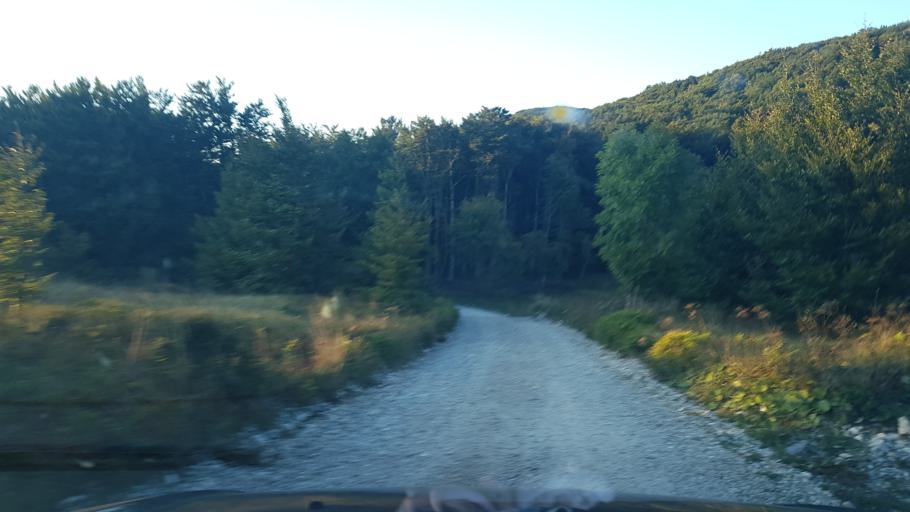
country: SI
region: Vipava
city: Vipava
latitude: 45.7729
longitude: 14.0502
